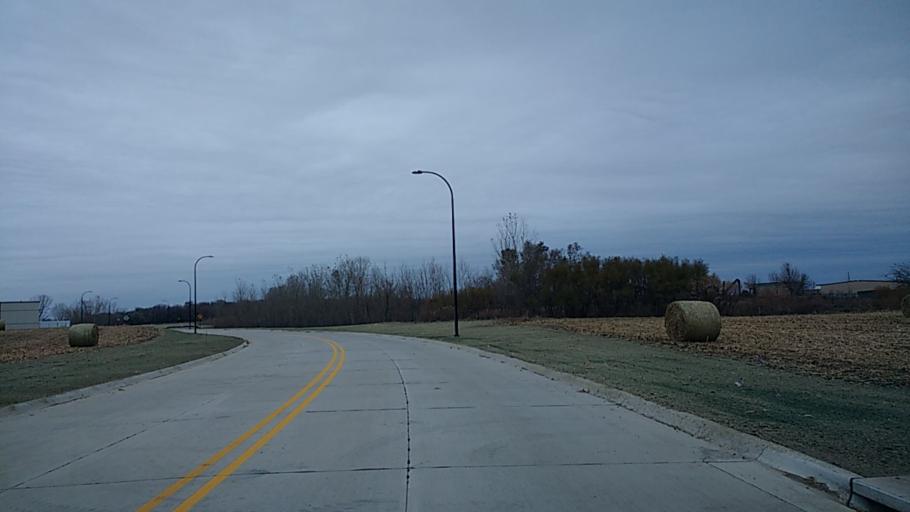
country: US
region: Iowa
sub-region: Woodbury County
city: Sergeant Bluff
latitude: 42.4172
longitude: -96.3728
